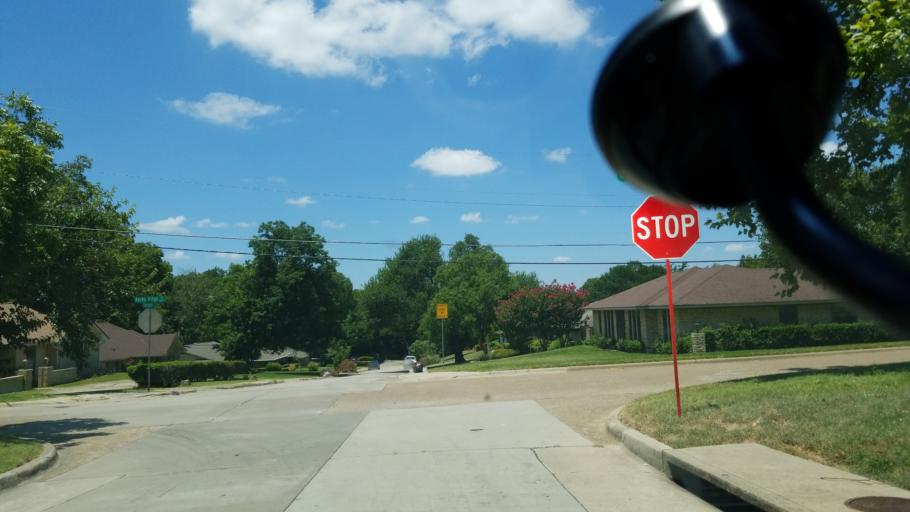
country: US
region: Texas
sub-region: Dallas County
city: Cockrell Hill
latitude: 32.6800
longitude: -96.8191
